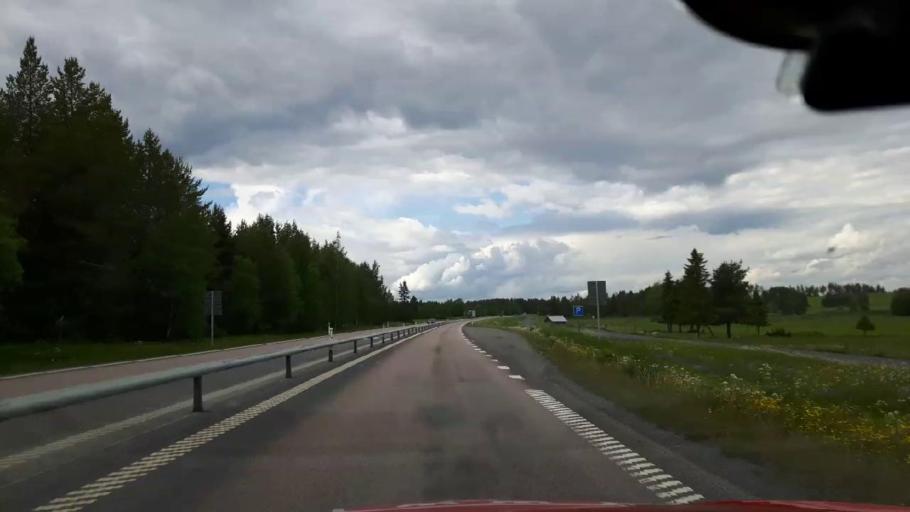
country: SE
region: Jaemtland
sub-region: OEstersunds Kommun
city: Ostersund
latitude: 63.2575
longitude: 14.5579
